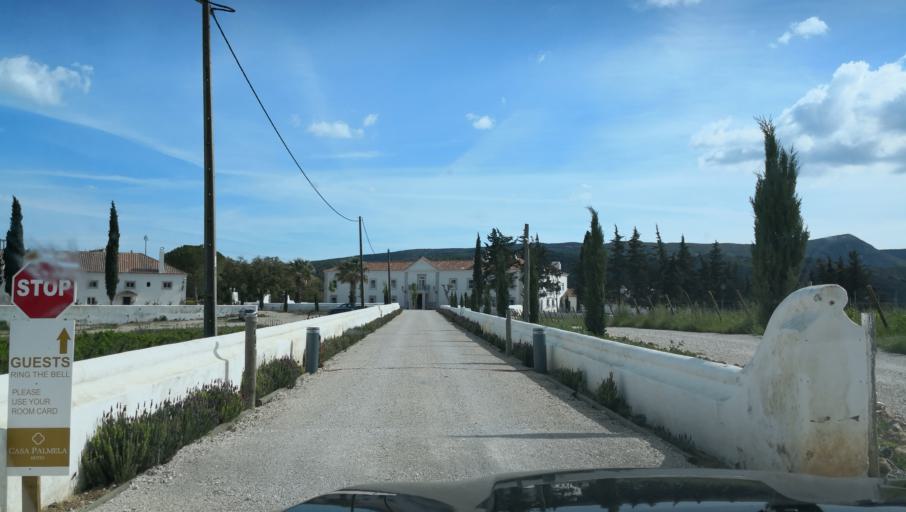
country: PT
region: Setubal
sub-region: Palmela
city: Quinta do Anjo
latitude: 38.5237
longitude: -8.9455
